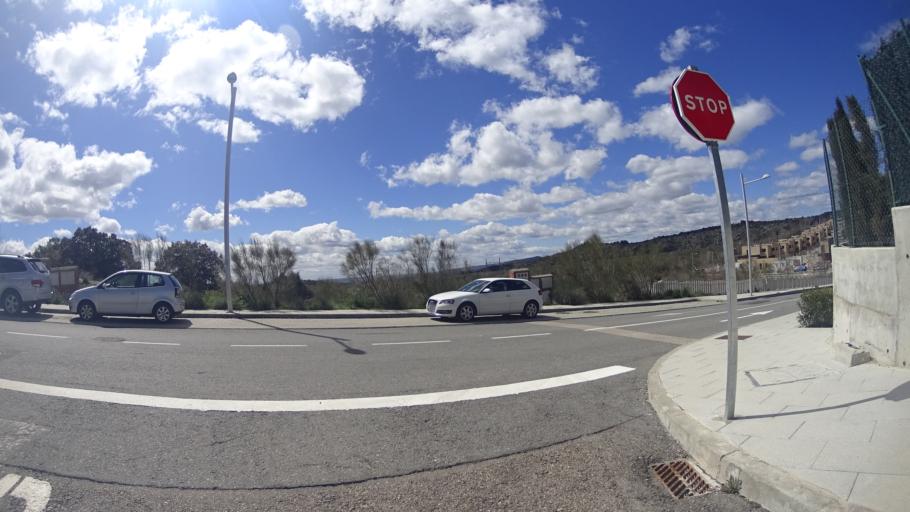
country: ES
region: Madrid
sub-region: Provincia de Madrid
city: Torrelodones
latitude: 40.5629
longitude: -3.9171
